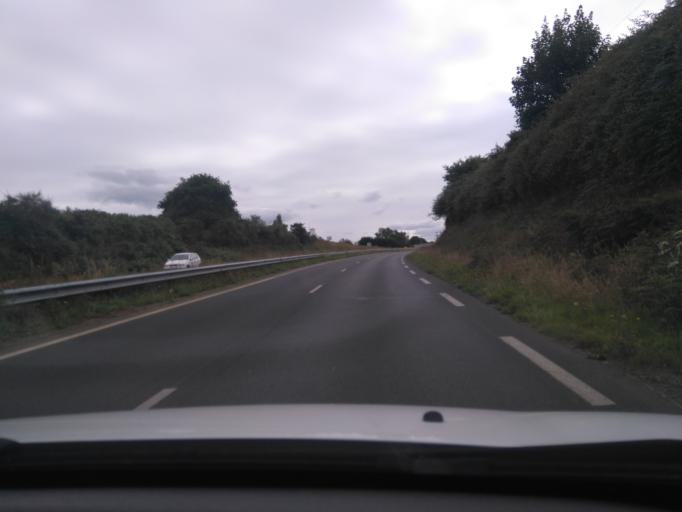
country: FR
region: Brittany
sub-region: Departement des Cotes-d'Armor
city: Saint-Quay-Perros
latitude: 48.7920
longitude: -3.4422
